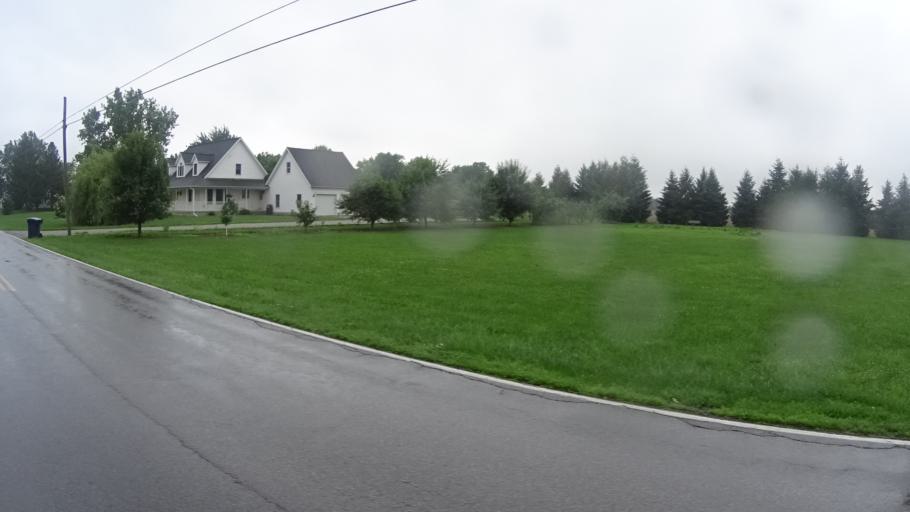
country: US
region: Ohio
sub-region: Huron County
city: Bellevue
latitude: 41.2879
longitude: -82.8414
